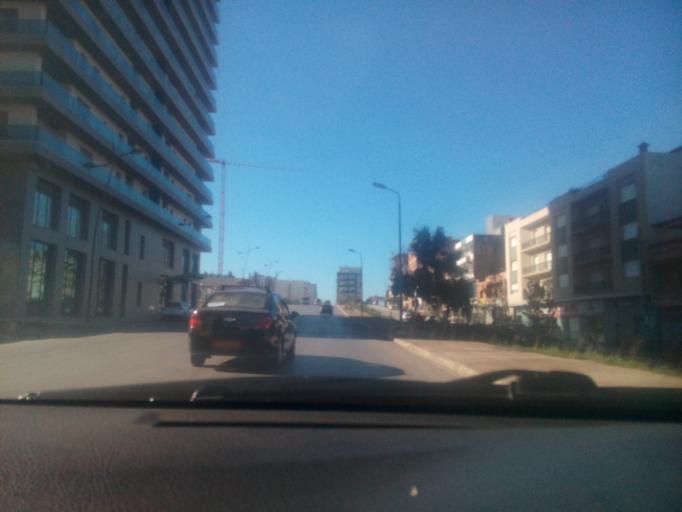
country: DZ
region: Oran
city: Bir el Djir
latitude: 35.7233
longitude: -0.5771
